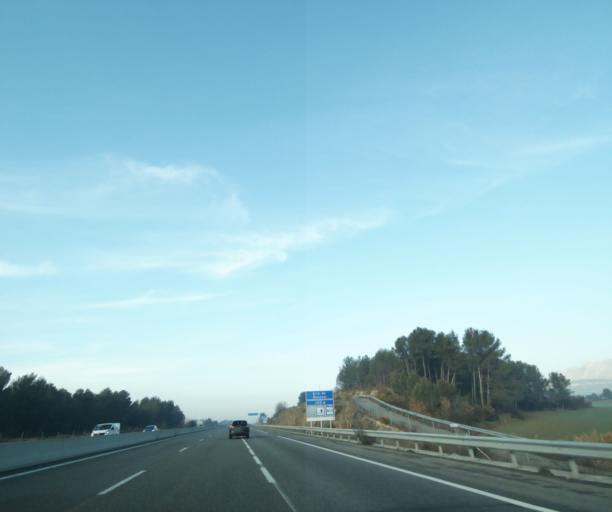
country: FR
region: Provence-Alpes-Cote d'Azur
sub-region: Departement des Bouches-du-Rhone
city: Peynier
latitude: 43.4702
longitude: 5.6509
